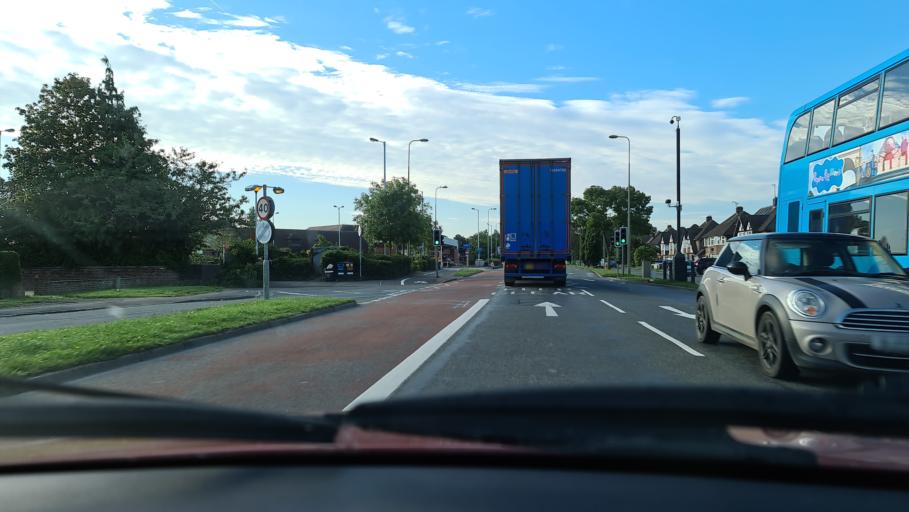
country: GB
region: England
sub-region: Oxfordshire
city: Kidlington
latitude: 51.8103
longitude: -1.2792
